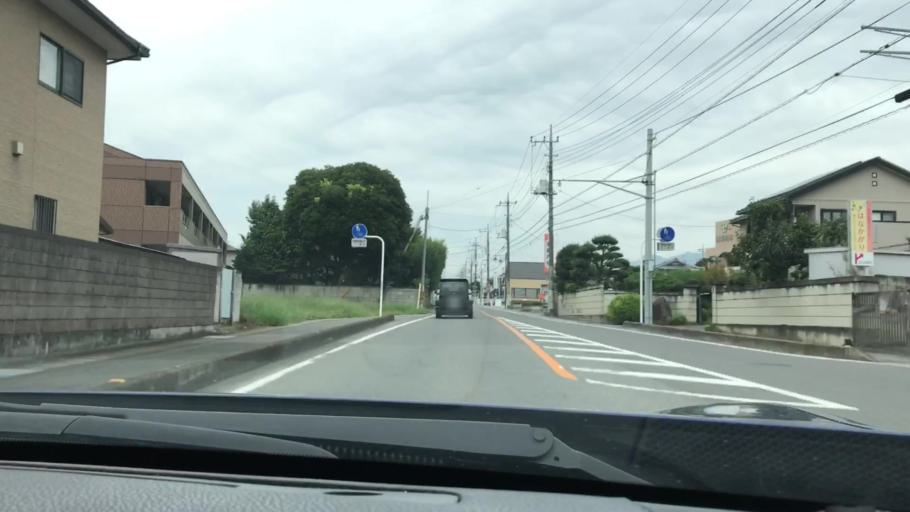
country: JP
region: Gunma
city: Kanekomachi
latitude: 36.3953
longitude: 139.0069
